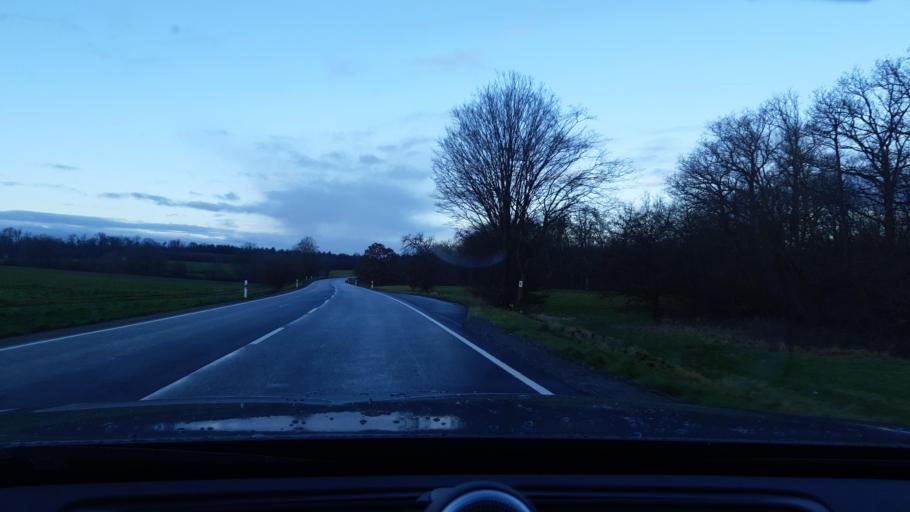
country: DE
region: Baden-Wuerttemberg
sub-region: Karlsruhe Region
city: Maulbronn
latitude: 48.9907
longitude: 8.8236
